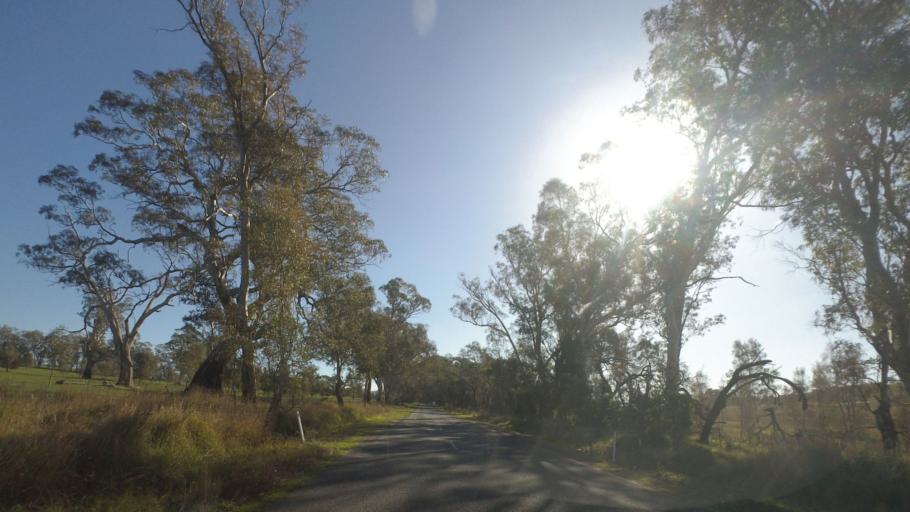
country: AU
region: Victoria
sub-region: Mount Alexander
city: Castlemaine
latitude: -36.9562
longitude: 144.3466
